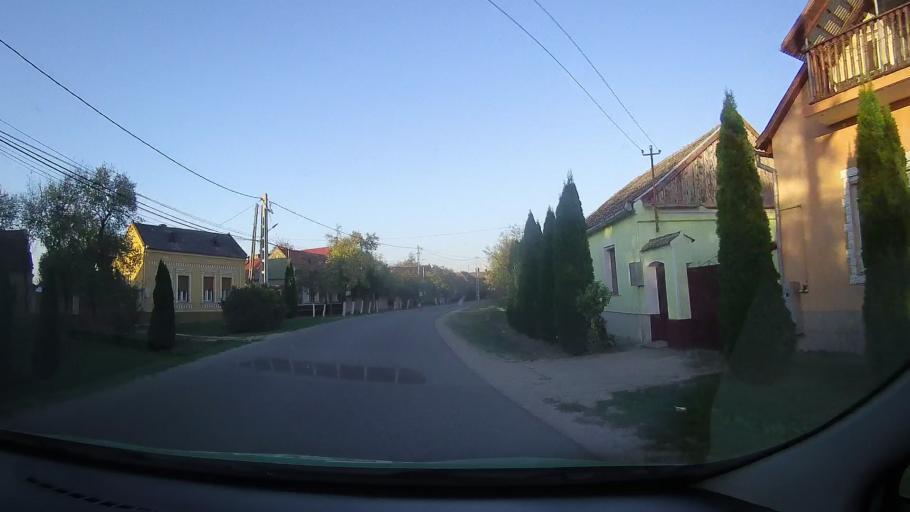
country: RO
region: Bihor
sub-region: Comuna Salard
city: Salard
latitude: 47.2275
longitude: 22.0290
